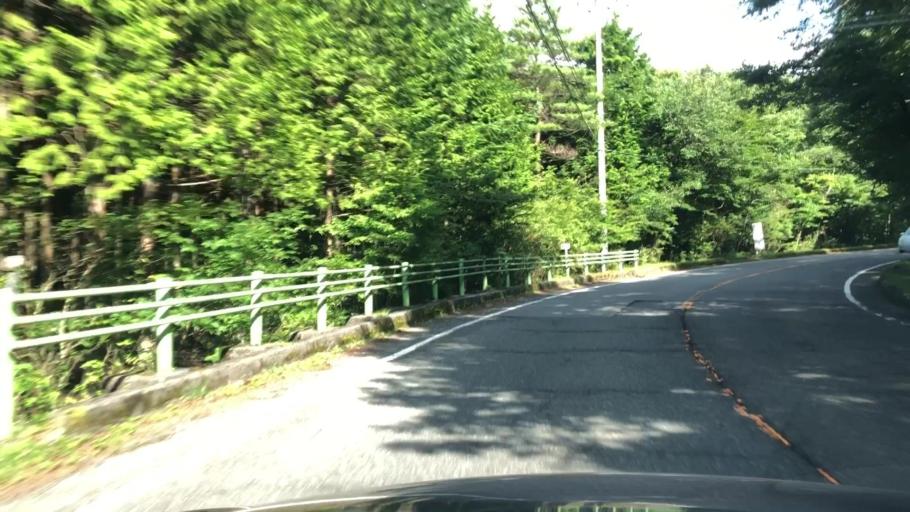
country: JP
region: Shizuoka
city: Gotemba
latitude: 35.3327
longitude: 138.8239
